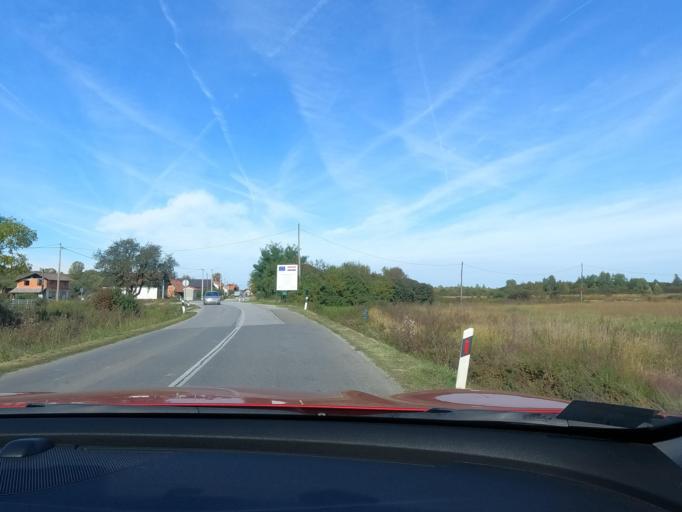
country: HR
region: Sisacko-Moslavacka
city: Petrinja
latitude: 45.4127
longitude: 16.2962
